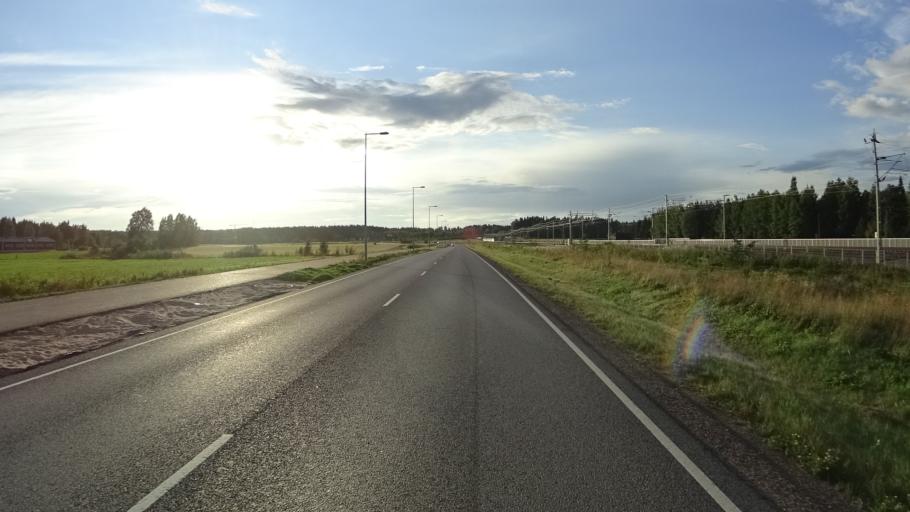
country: FI
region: Uusimaa
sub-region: Helsinki
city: Teekkarikylae
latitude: 60.3144
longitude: 24.8811
